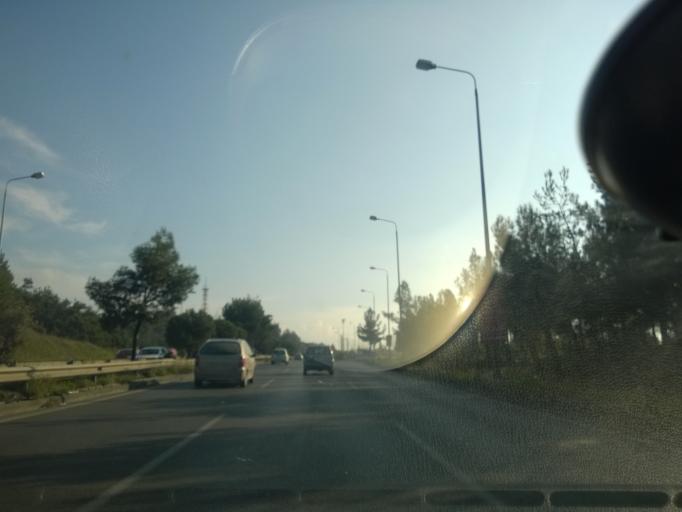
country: GR
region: Central Macedonia
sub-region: Nomos Thessalonikis
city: Agios Pavlos
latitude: 40.6460
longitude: 22.9684
